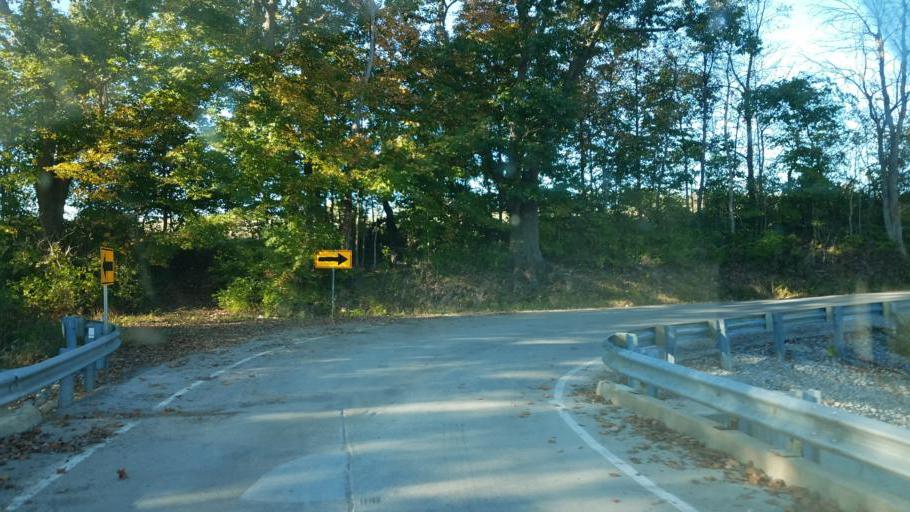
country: US
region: Kentucky
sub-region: Fleming County
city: Flemingsburg
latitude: 38.4903
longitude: -83.5939
